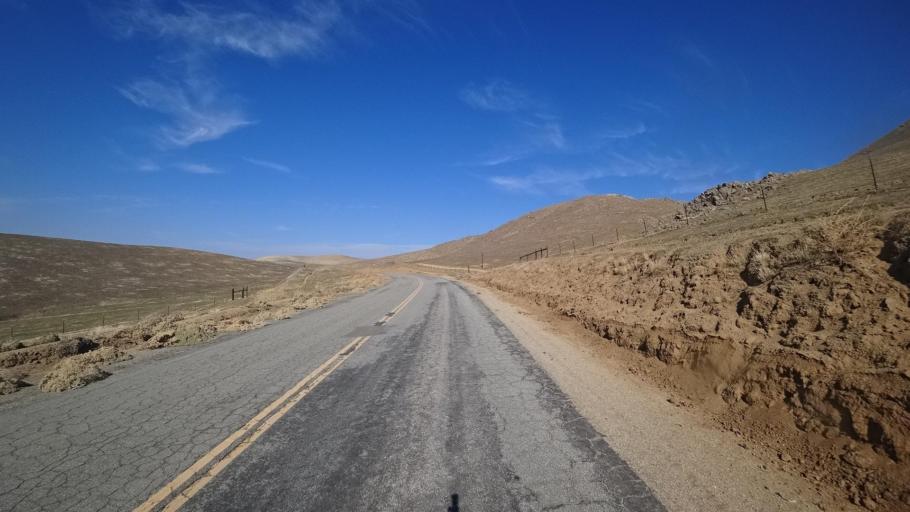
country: US
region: California
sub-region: Kern County
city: Oildale
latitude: 35.4655
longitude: -118.8258
